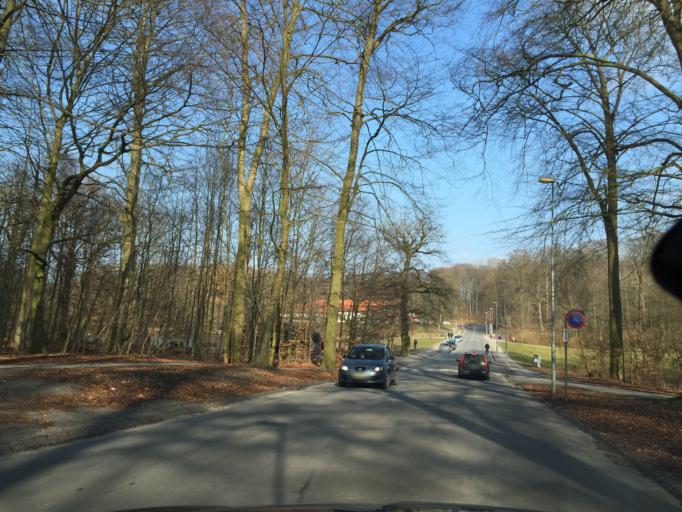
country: DK
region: South Denmark
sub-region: Odense Kommune
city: Odense
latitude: 55.3694
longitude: 10.3806
